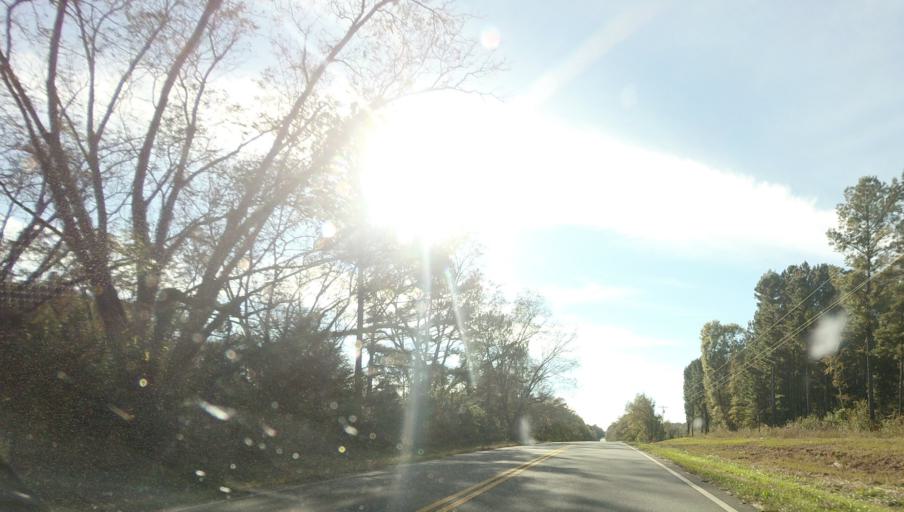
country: US
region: Georgia
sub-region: Talbot County
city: Talbotton
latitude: 32.6945
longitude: -84.4565
